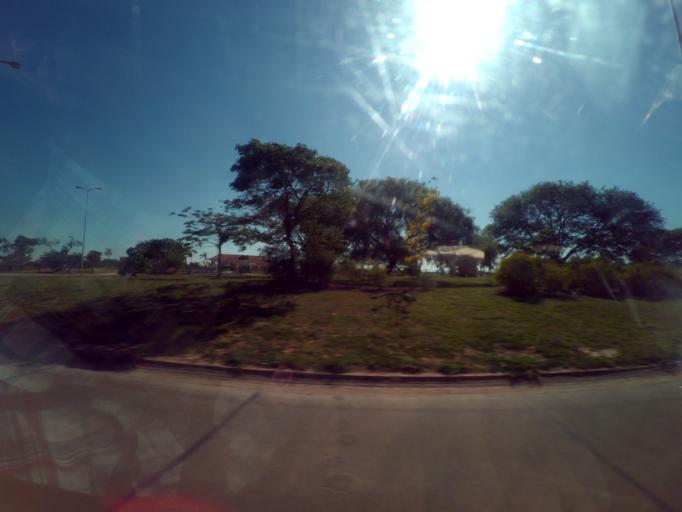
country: BO
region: Santa Cruz
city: Santa Cruz de la Sierra
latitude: -17.7548
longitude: -63.2162
